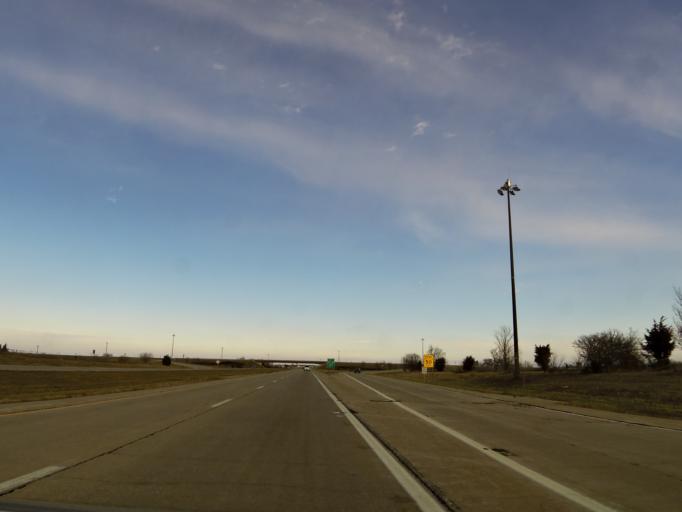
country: US
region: Illinois
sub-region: LaSalle County
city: Oglesby
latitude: 41.2607
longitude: -89.0812
